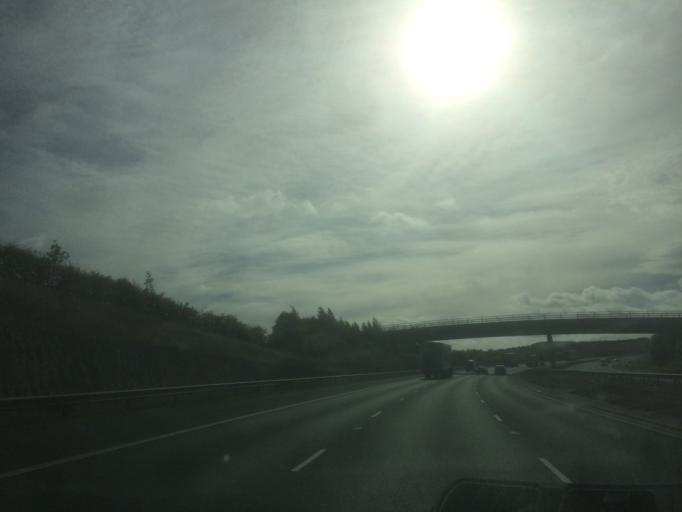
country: GB
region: England
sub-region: City and Borough of Leeds
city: Aberford
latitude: 53.7967
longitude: -1.3240
